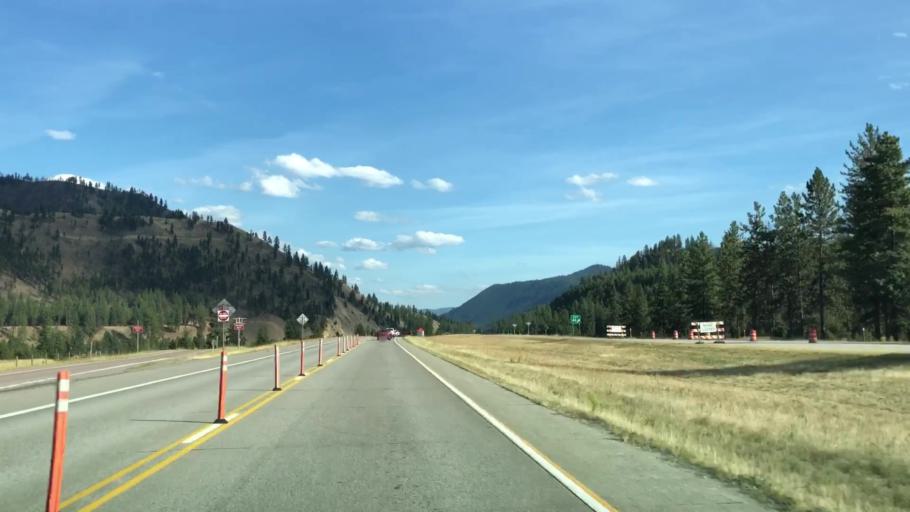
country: US
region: Montana
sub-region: Mineral County
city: Superior
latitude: 47.2284
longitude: -114.9743
